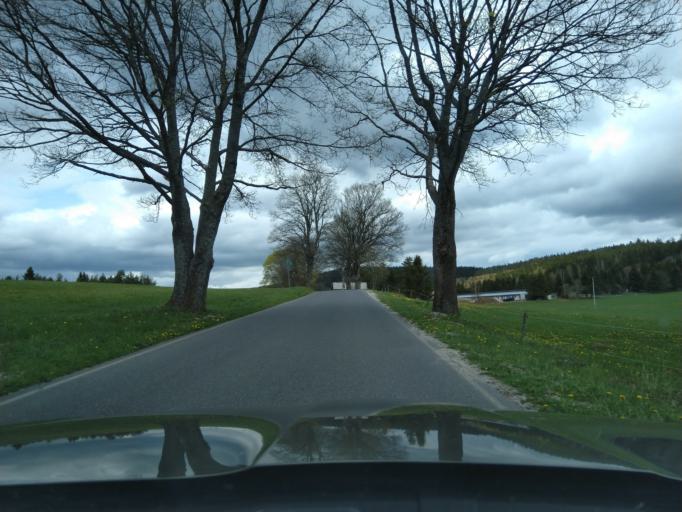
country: CZ
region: Jihocesky
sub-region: Okres Prachatice
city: Borova Lada
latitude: 49.0003
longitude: 13.6712
